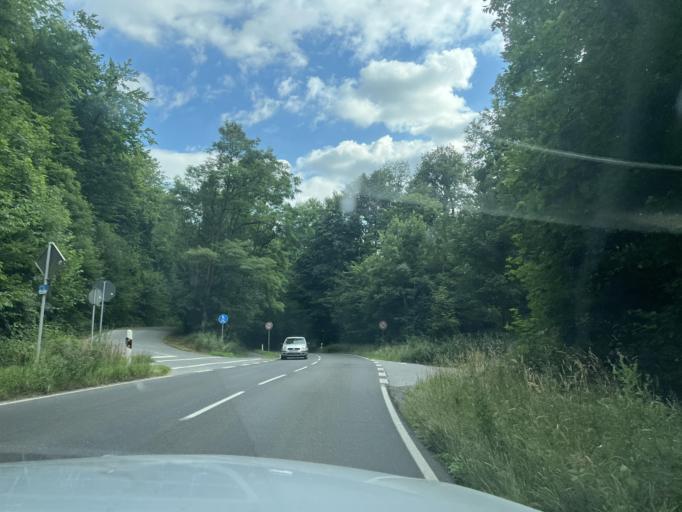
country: DE
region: North Rhine-Westphalia
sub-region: Regierungsbezirk Koln
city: Bergheim
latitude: 50.9427
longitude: 6.6941
